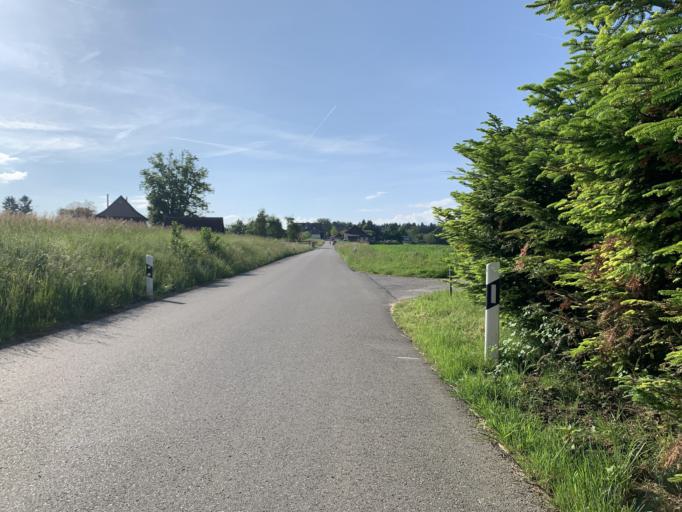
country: CH
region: Zurich
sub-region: Bezirk Hinwil
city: Wetzikon / Unter-Wetzikon
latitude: 47.2966
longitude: 8.8005
